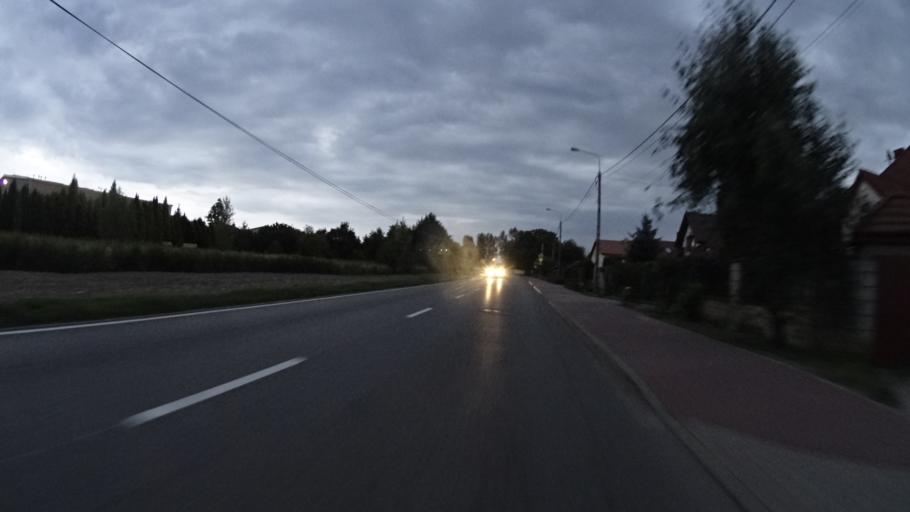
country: PL
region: Masovian Voivodeship
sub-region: Powiat warszawski zachodni
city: Babice
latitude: 52.2261
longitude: 20.8588
